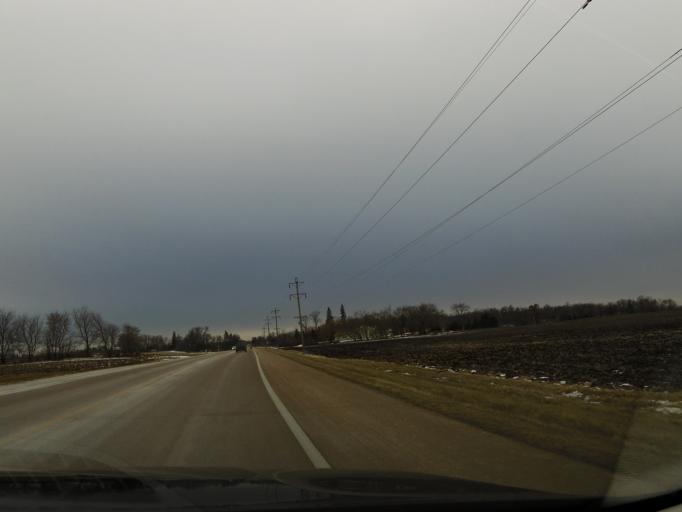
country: US
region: Minnesota
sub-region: Carver County
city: Watertown
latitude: 44.9232
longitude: -93.8287
